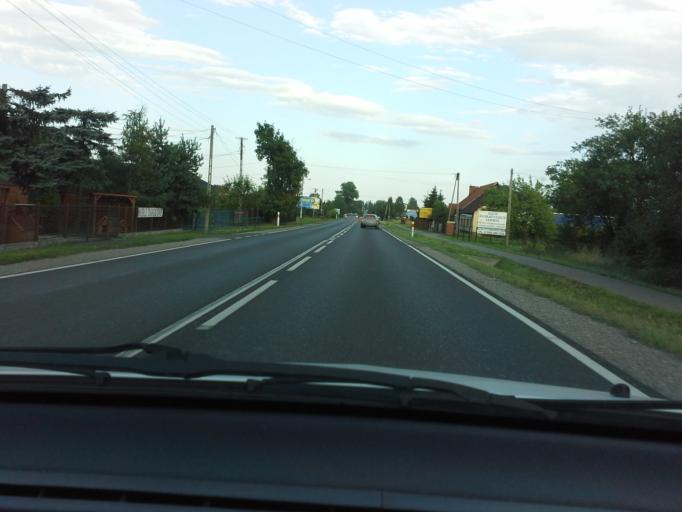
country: PL
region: Lesser Poland Voivodeship
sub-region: Powiat krakowski
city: Wola Filipowska
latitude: 50.1309
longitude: 19.5975
